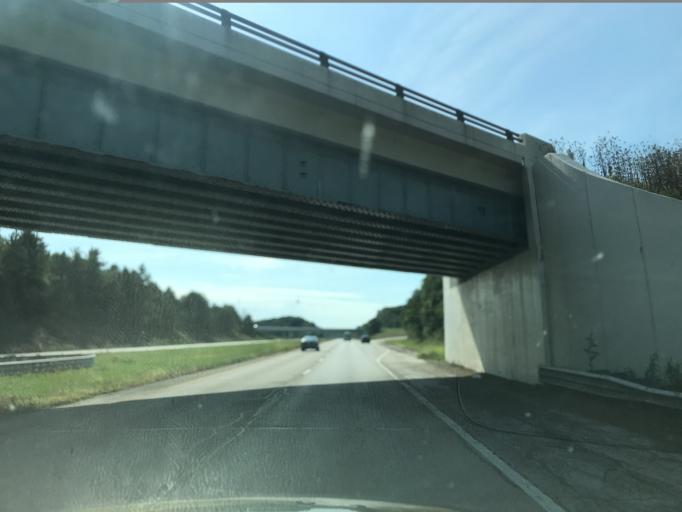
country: US
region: Ohio
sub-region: Ashtabula County
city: Edgewood
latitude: 41.8666
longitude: -80.7625
